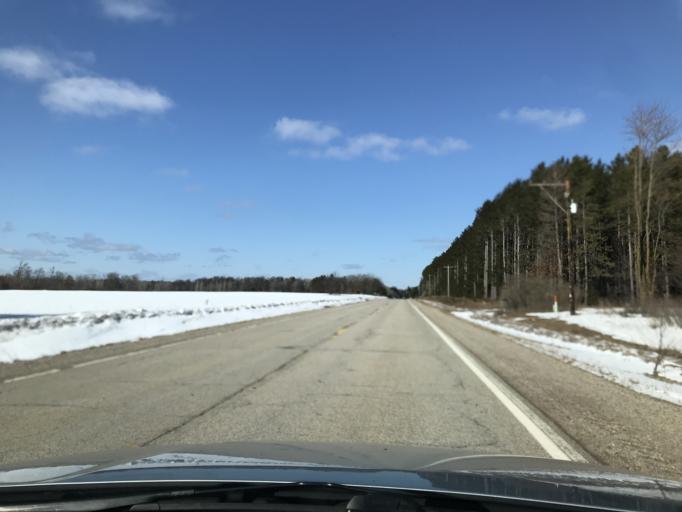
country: US
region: Wisconsin
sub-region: Marinette County
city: Peshtigo
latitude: 45.3214
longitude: -88.1021
